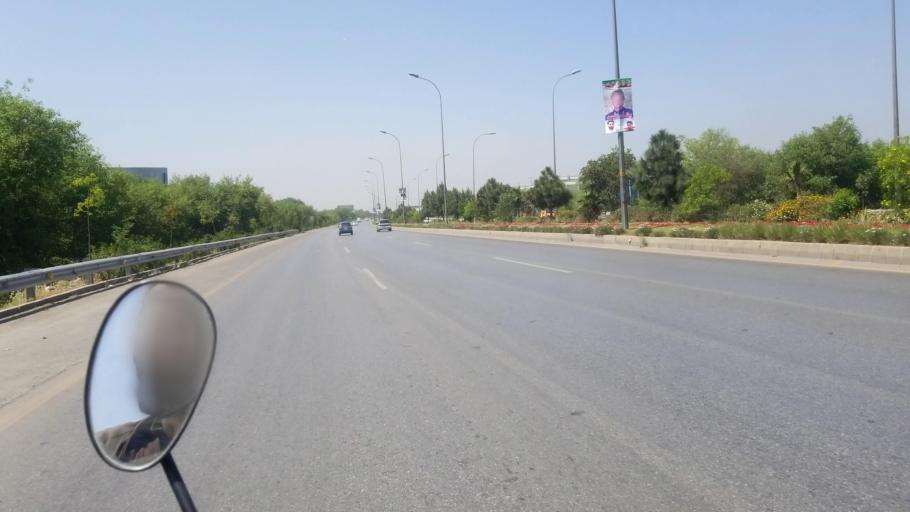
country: PK
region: Khyber Pakhtunkhwa
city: Peshawar
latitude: 34.0286
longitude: 71.6597
